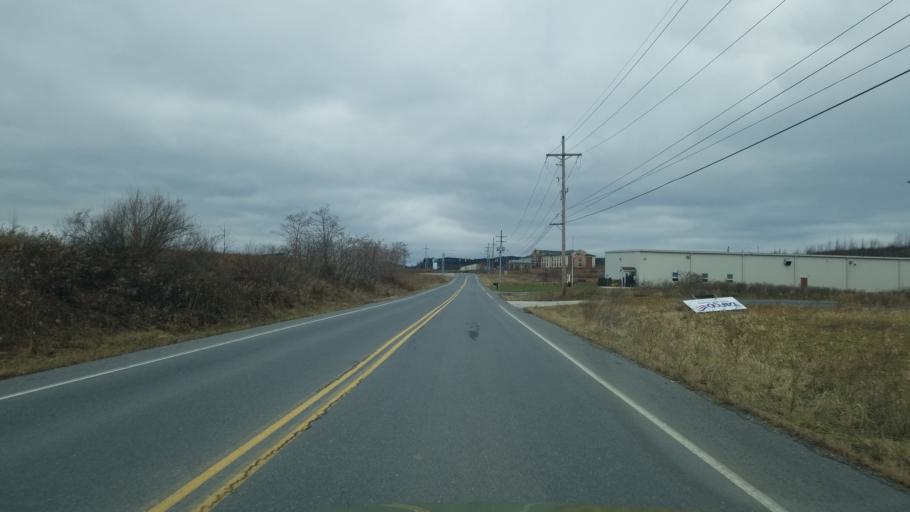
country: US
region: Pennsylvania
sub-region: Clearfield County
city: Clearfield
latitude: 41.0316
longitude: -78.3899
